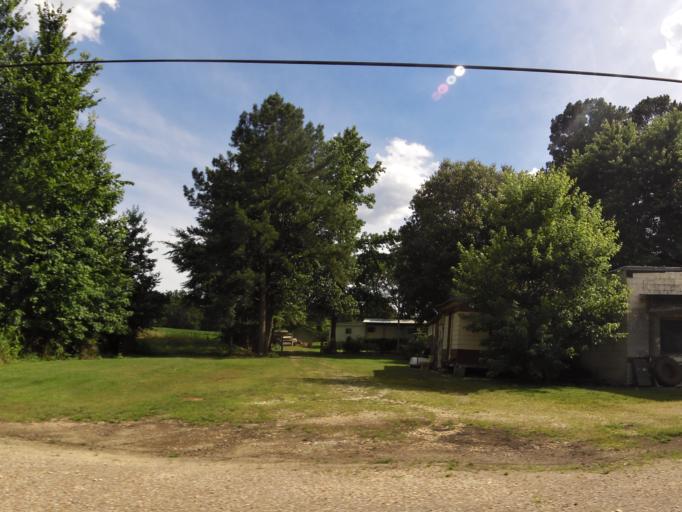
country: US
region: Tennessee
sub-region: Carroll County
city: Huntingdon
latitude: 36.0043
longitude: -88.5381
